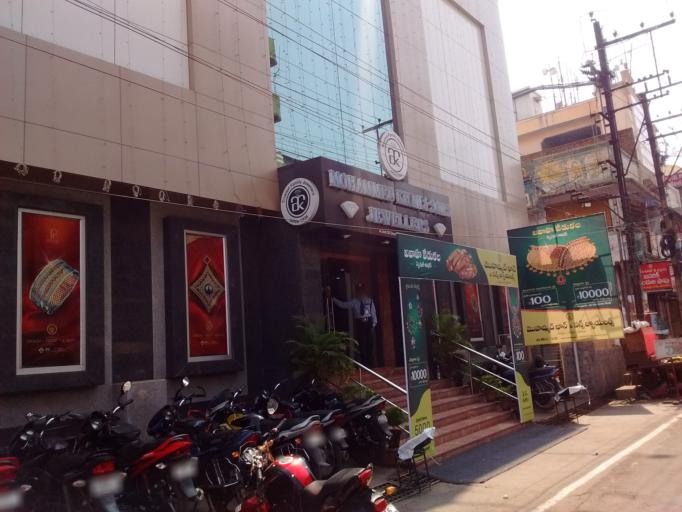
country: IN
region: Andhra Pradesh
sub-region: Krishna
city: Vijayawada
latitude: 16.5101
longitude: 80.6265
